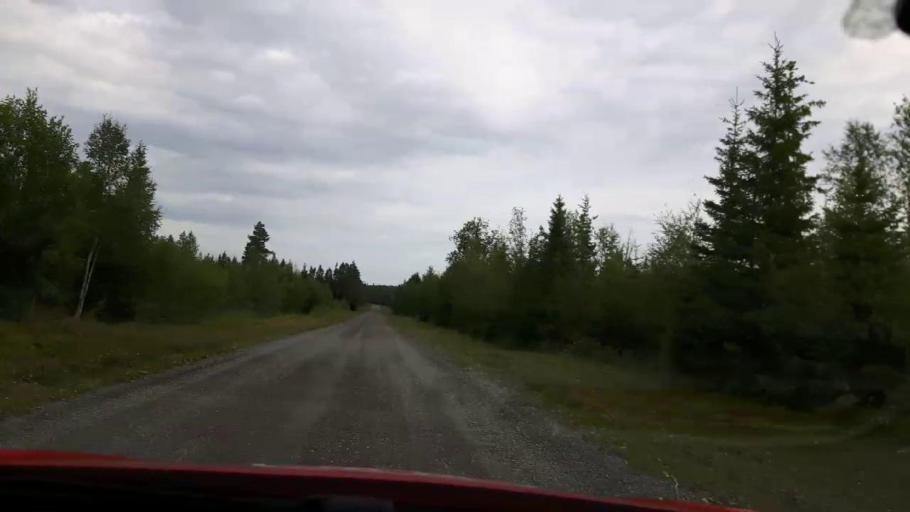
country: SE
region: Jaemtland
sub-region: Stroemsunds Kommun
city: Stroemsund
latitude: 63.7488
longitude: 15.5898
